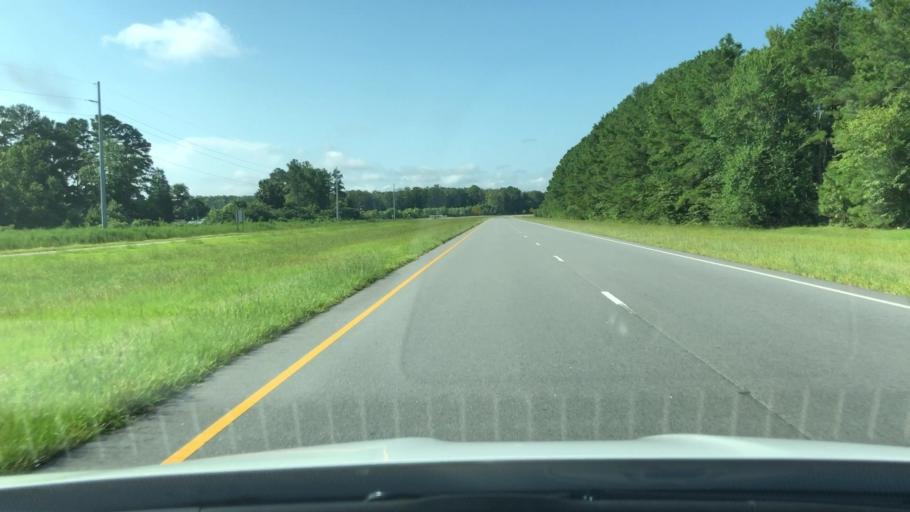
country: US
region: North Carolina
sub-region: Pasquotank County
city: Elizabeth City
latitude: 36.4405
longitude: -76.3391
